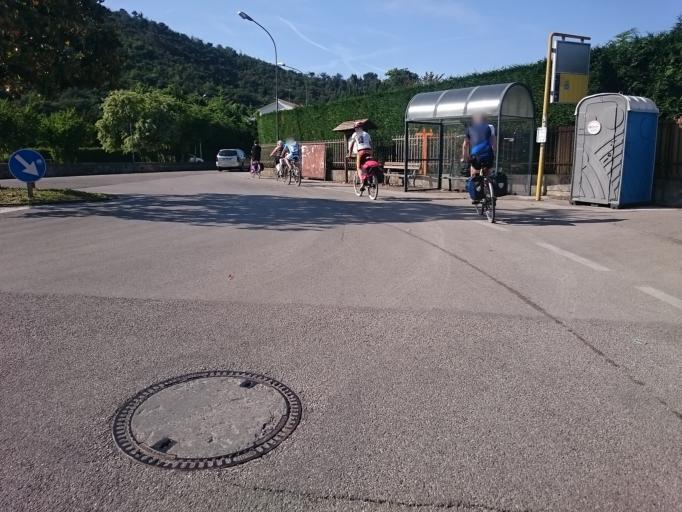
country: IT
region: Veneto
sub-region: Provincia di Padova
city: Torreglia
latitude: 45.3499
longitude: 11.7585
